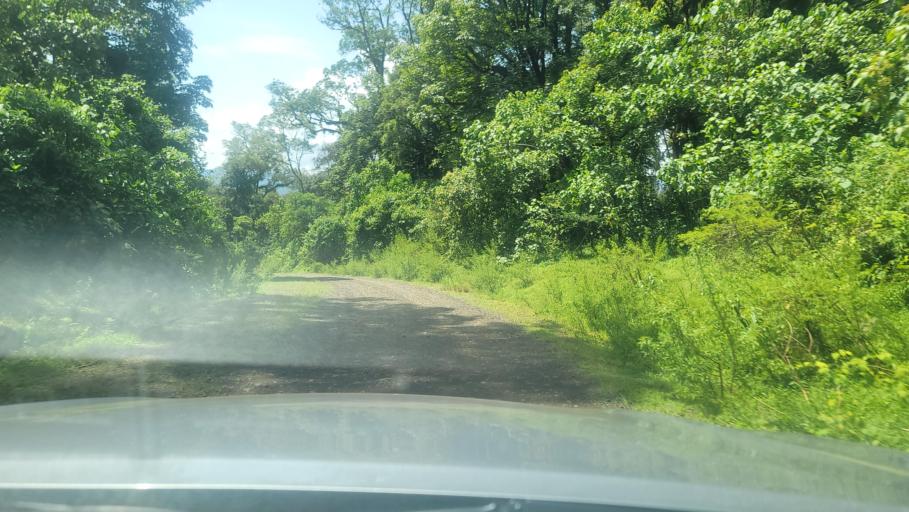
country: ET
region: Southern Nations, Nationalities, and People's Region
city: Bonga
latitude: 7.6637
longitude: 36.2439
